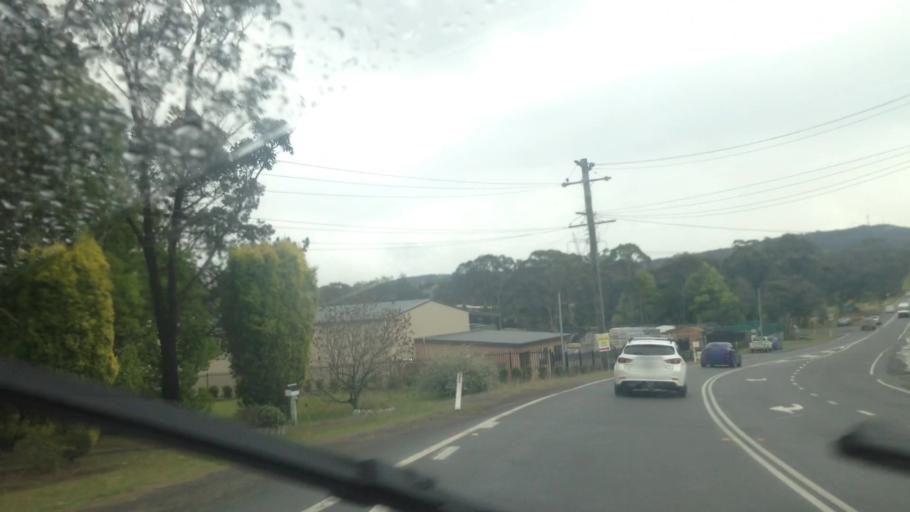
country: AU
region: New South Wales
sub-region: Wyong Shire
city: Charmhaven
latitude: -33.1756
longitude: 151.4807
